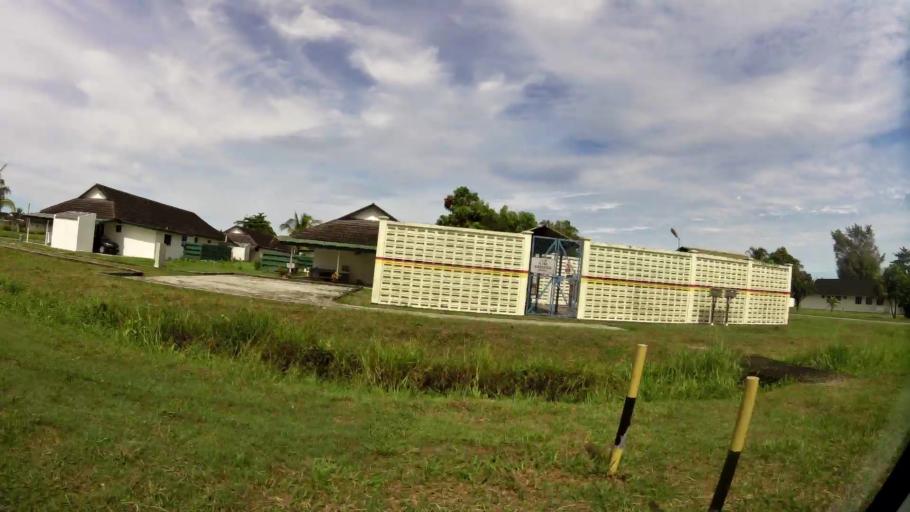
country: BN
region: Belait
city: Seria
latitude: 4.6093
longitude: 114.3237
